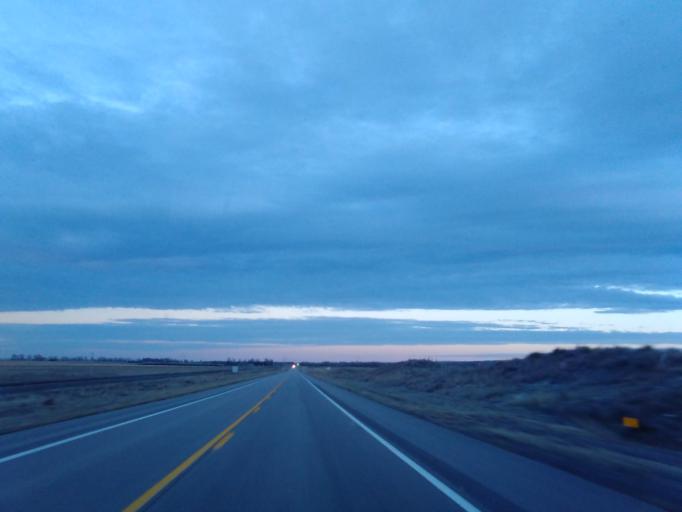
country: US
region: Nebraska
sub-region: Garden County
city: Oshkosh
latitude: 41.3724
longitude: -102.2485
